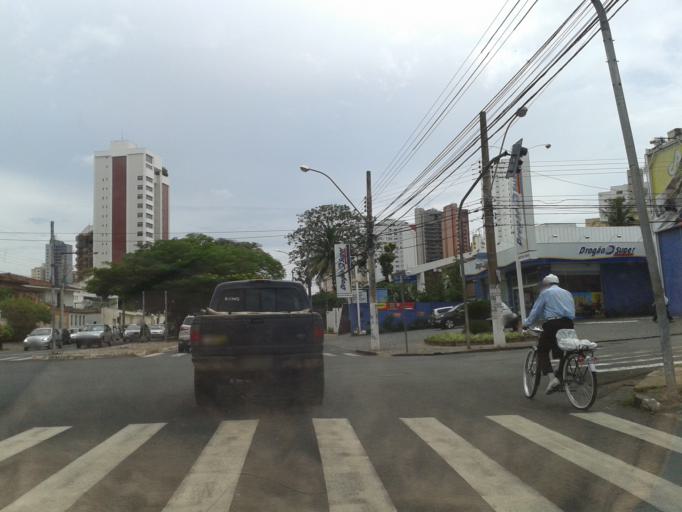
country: BR
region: Minas Gerais
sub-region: Uberlandia
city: Uberlandia
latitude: -18.9222
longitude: -48.2884
